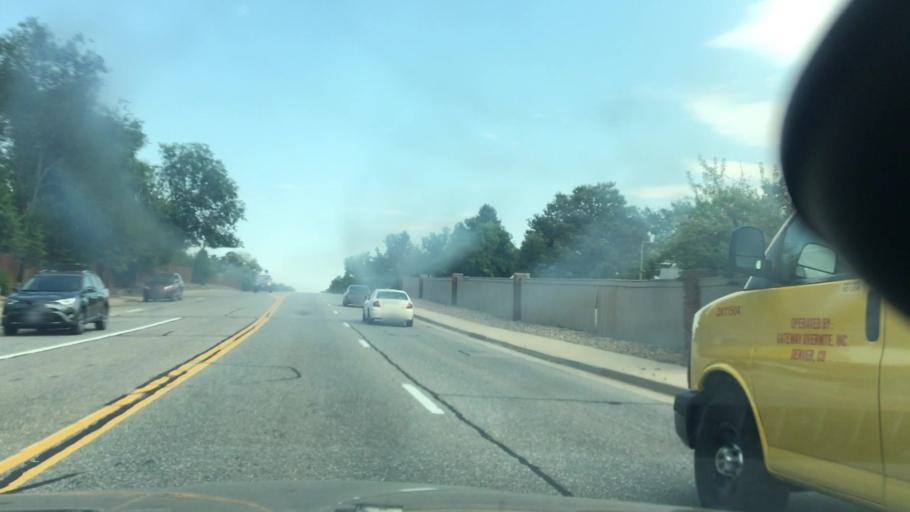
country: US
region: Colorado
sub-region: Arapahoe County
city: Castlewood
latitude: 39.5805
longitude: -104.9035
